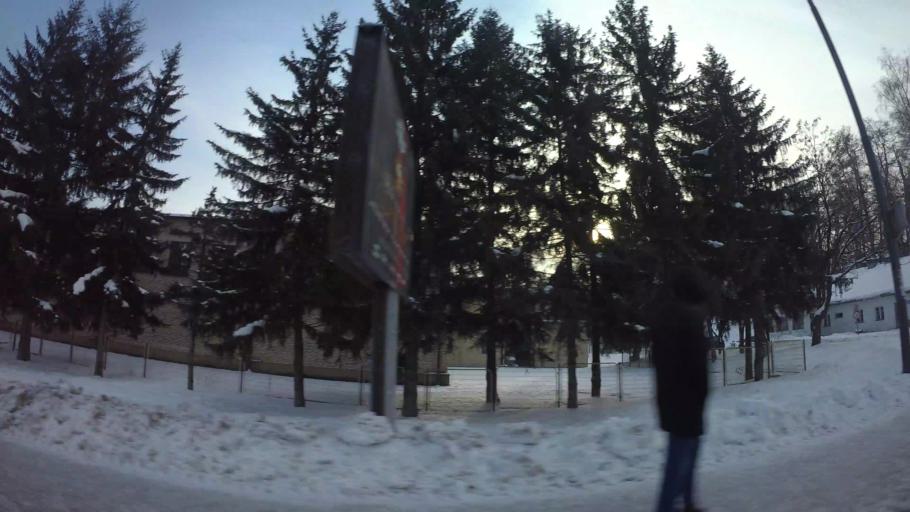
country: BA
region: Federation of Bosnia and Herzegovina
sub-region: Kanton Sarajevo
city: Sarajevo
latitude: 43.8256
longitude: 18.3644
